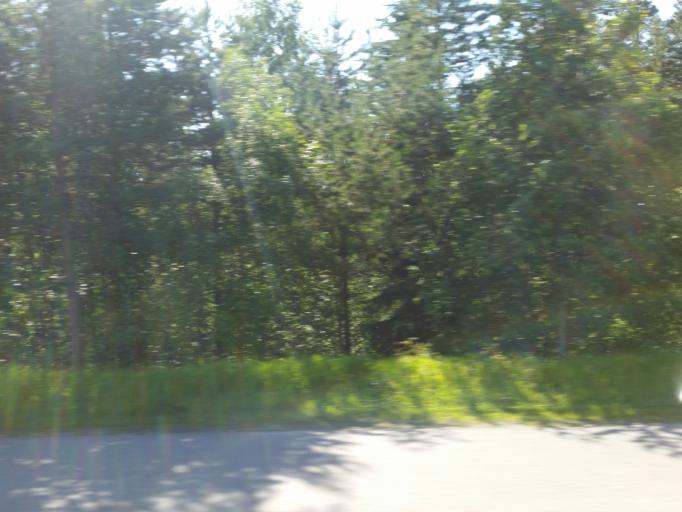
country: FI
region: Northern Savo
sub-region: Kuopio
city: Kuopio
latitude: 62.9014
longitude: 27.6753
